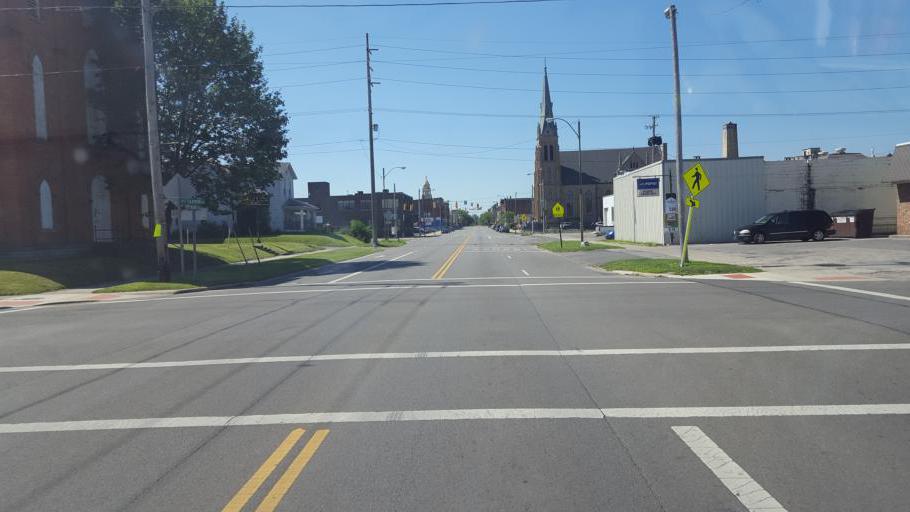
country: US
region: Ohio
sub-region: Marion County
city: Marion
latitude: 40.5937
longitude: -83.1292
